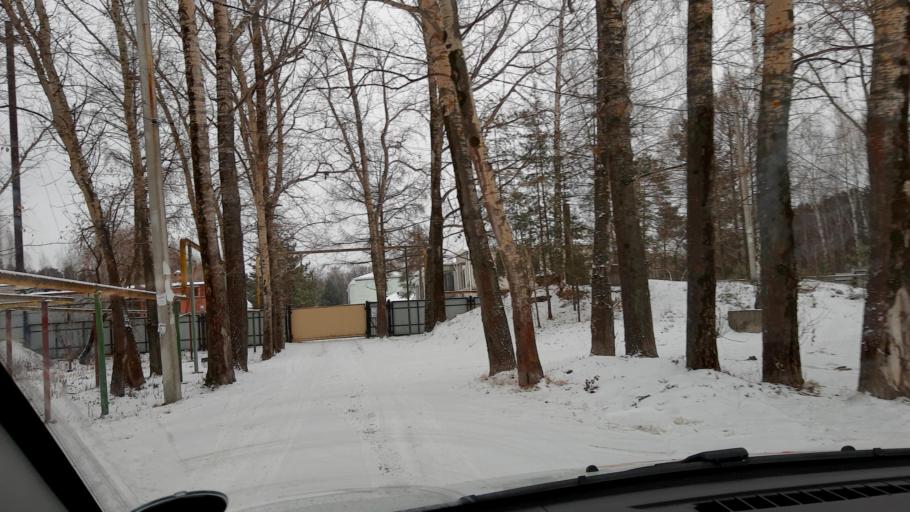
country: RU
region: Nizjnij Novgorod
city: Burevestnik
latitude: 56.1965
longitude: 43.7727
